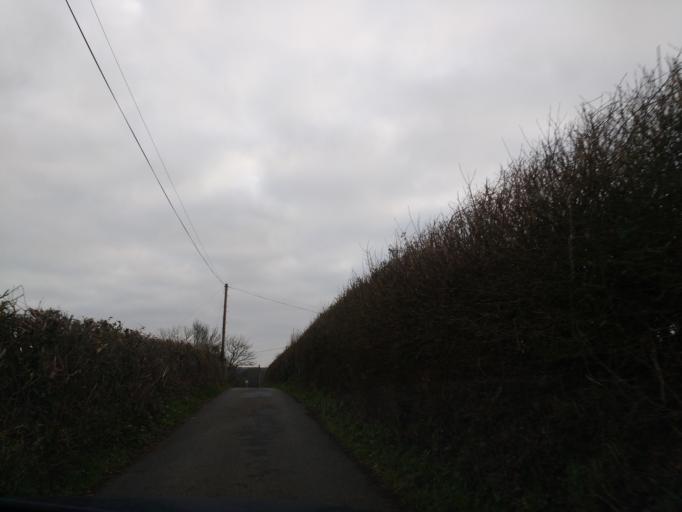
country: GB
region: England
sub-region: Isle of Wight
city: Shalfleet
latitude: 50.6887
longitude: -1.3955
